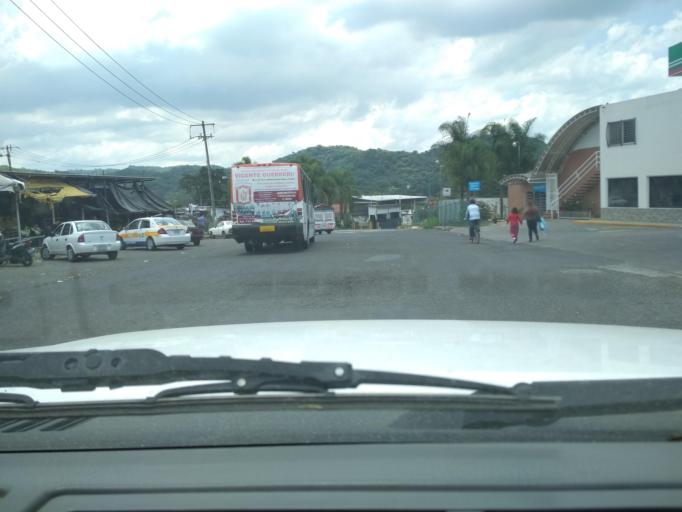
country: MX
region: Veracruz
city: Cordoba
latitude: 18.8848
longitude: -96.9206
